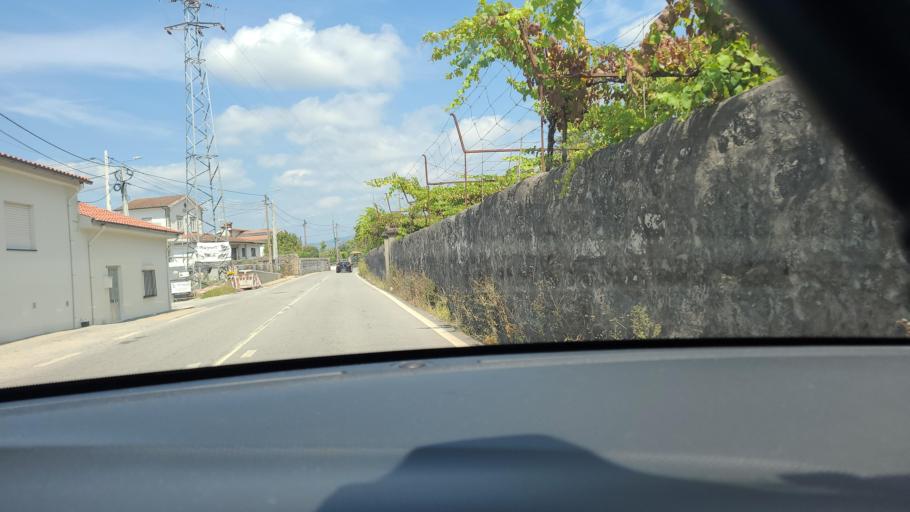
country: PT
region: Braga
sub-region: Braga
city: Adaufe
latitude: 41.5798
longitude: -8.4085
